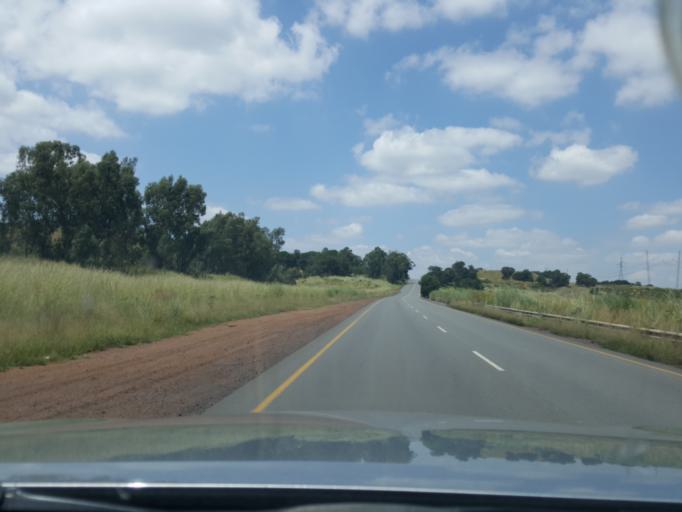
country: ZA
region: Mpumalanga
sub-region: Nkangala District Municipality
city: Witbank
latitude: -26.0140
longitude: 29.3703
